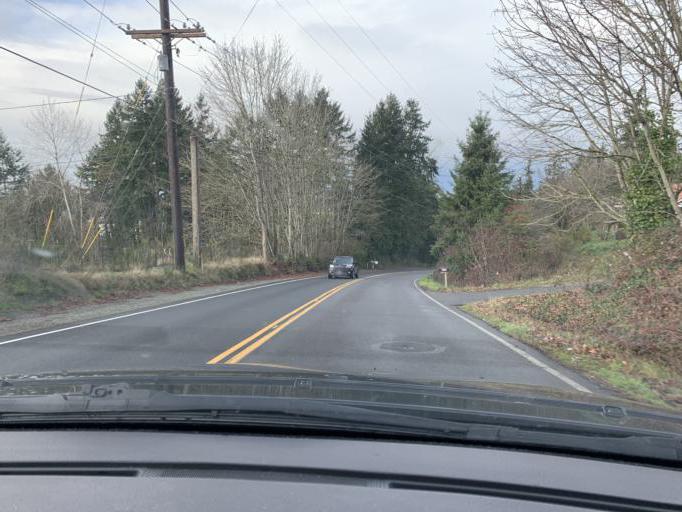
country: US
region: Washington
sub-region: Pierce County
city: Milton
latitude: 47.2391
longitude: -122.3231
